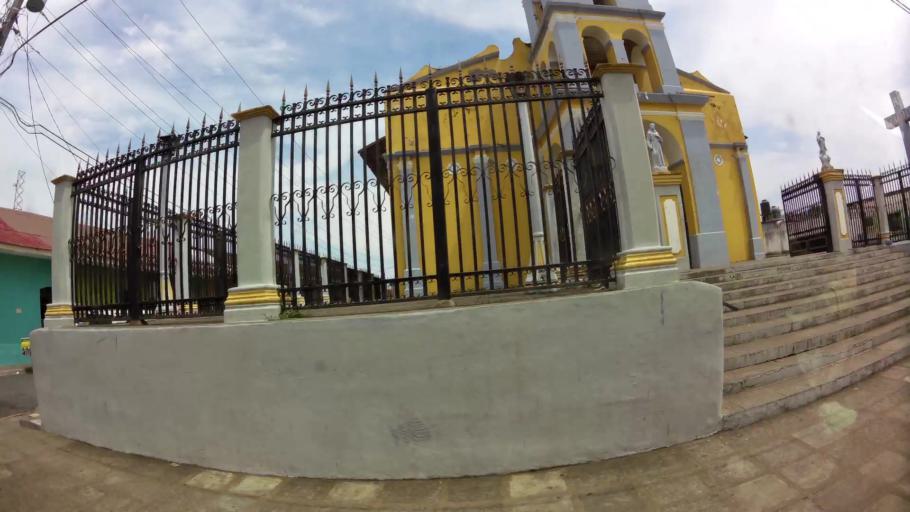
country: NI
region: Rivas
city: Rivas
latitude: 11.4377
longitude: -85.8313
